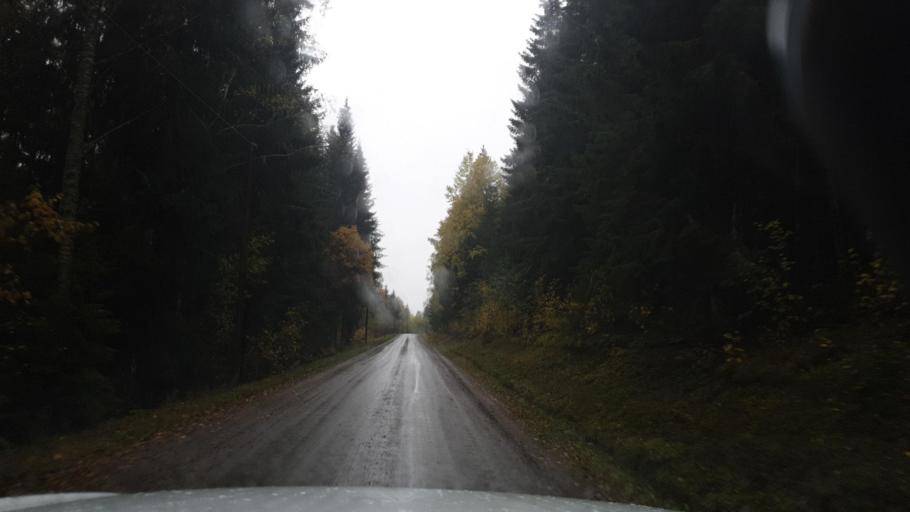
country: SE
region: Vaermland
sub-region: Eda Kommun
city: Amotfors
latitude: 59.7479
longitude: 12.2740
